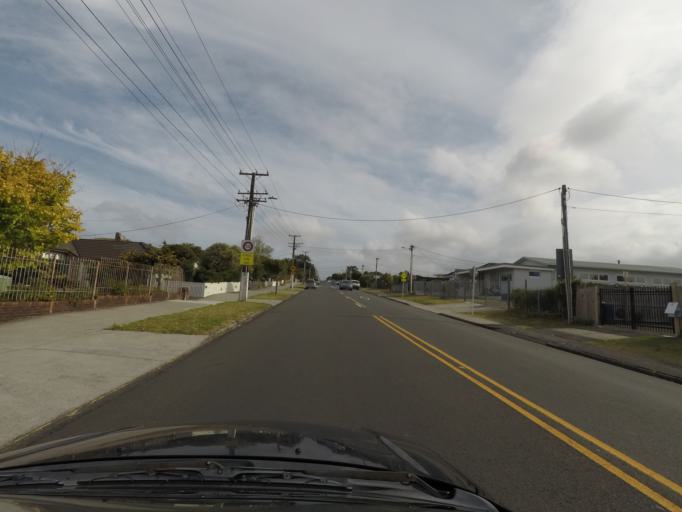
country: NZ
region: Auckland
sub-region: Auckland
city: Waitakere
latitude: -36.9010
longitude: 174.6662
